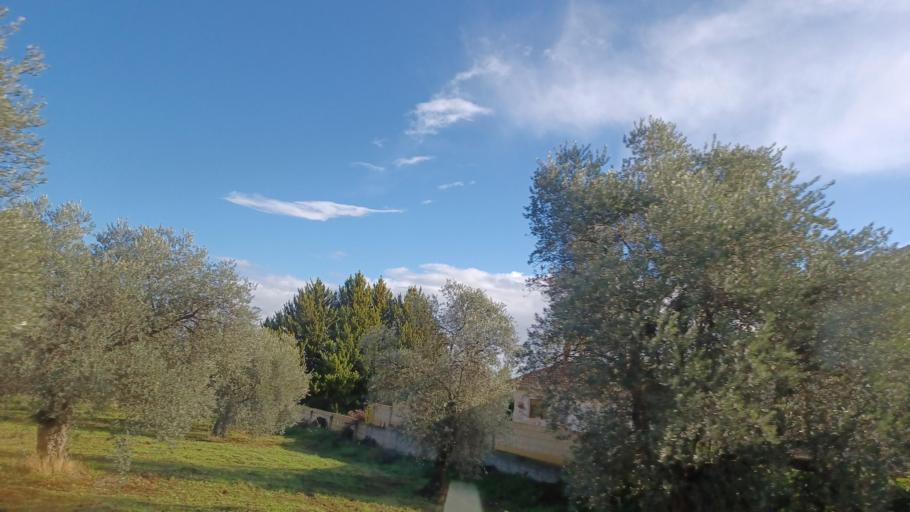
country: CY
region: Lefkosia
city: Lythrodontas
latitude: 34.9389
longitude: 33.2976
